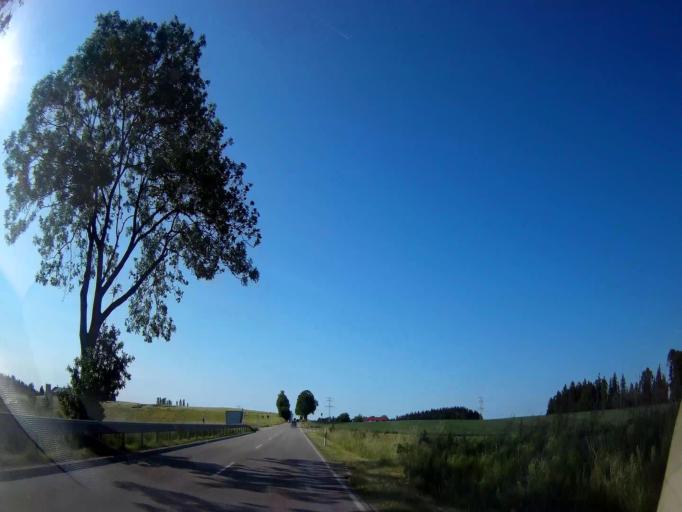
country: DE
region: Bavaria
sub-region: Lower Bavaria
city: Zeilarn
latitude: 48.3317
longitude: 12.8259
